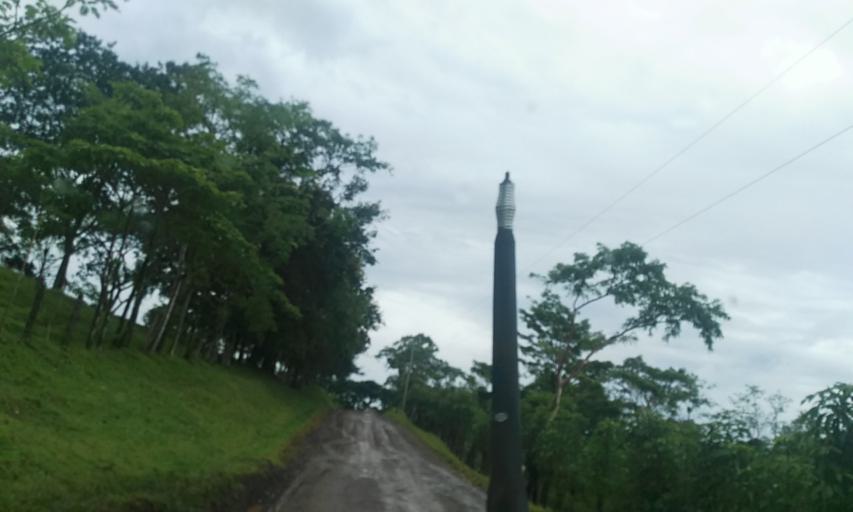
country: NI
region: Matagalpa
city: Rio Blanco
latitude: 12.9613
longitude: -85.1824
